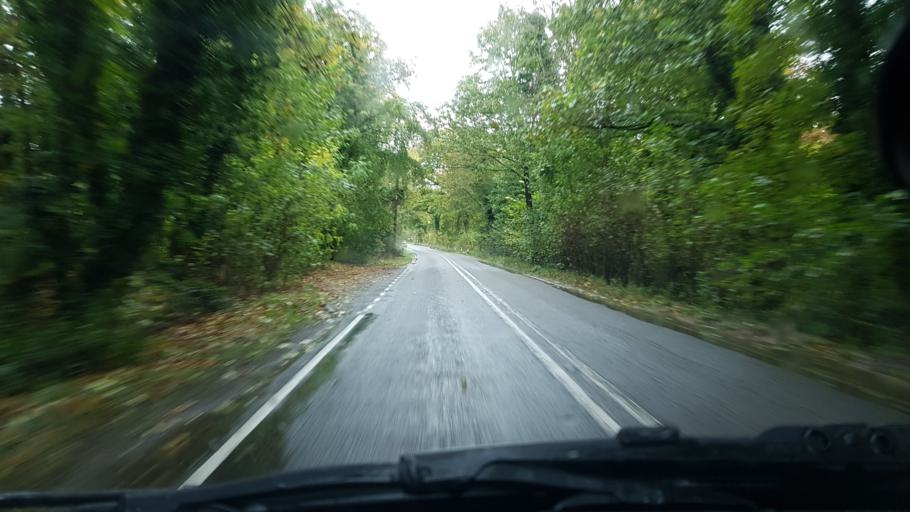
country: GB
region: England
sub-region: Oxfordshire
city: Ducklington
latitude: 51.7584
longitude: -1.4648
